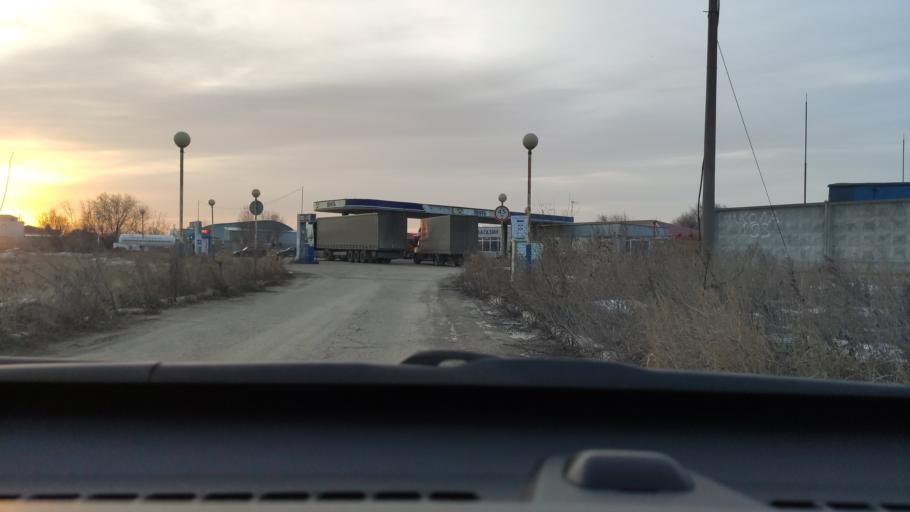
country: RU
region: Samara
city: Tol'yatti
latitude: 53.5772
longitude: 49.4061
